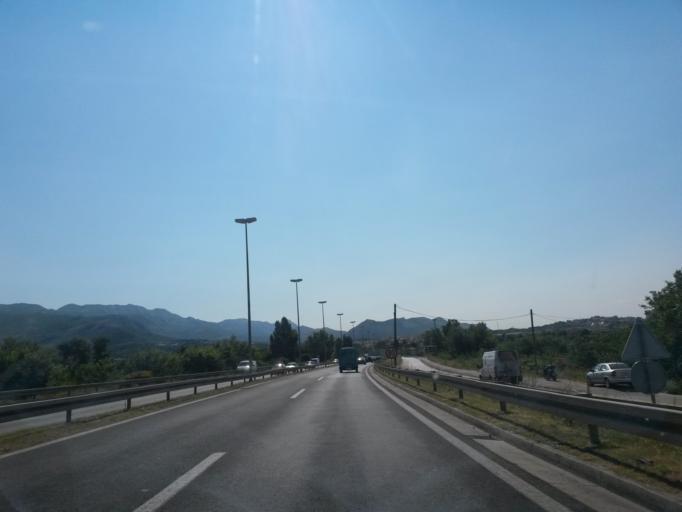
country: HR
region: Splitsko-Dalmatinska
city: Vranjic
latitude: 43.5368
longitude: 16.4768
